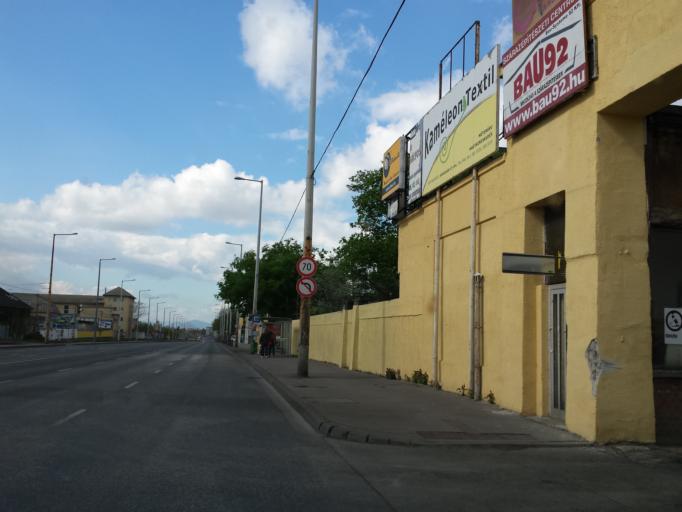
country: HU
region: Budapest
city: Budapest XX. keruelet
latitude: 47.4440
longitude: 19.0930
